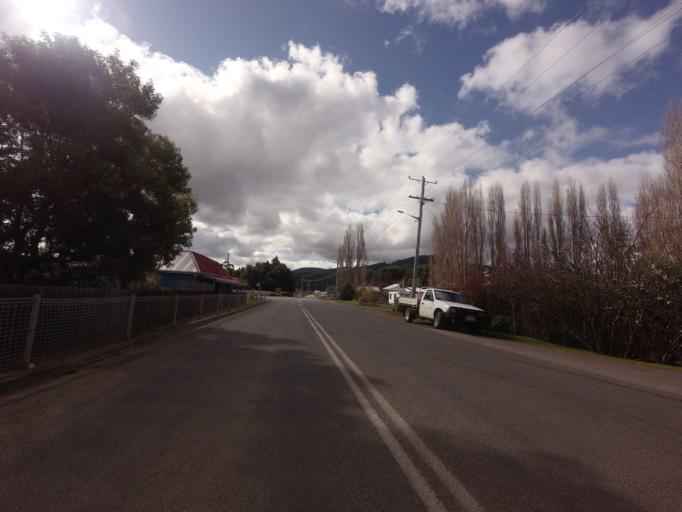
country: AU
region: Tasmania
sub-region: Huon Valley
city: Geeveston
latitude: -43.1676
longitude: 146.9261
